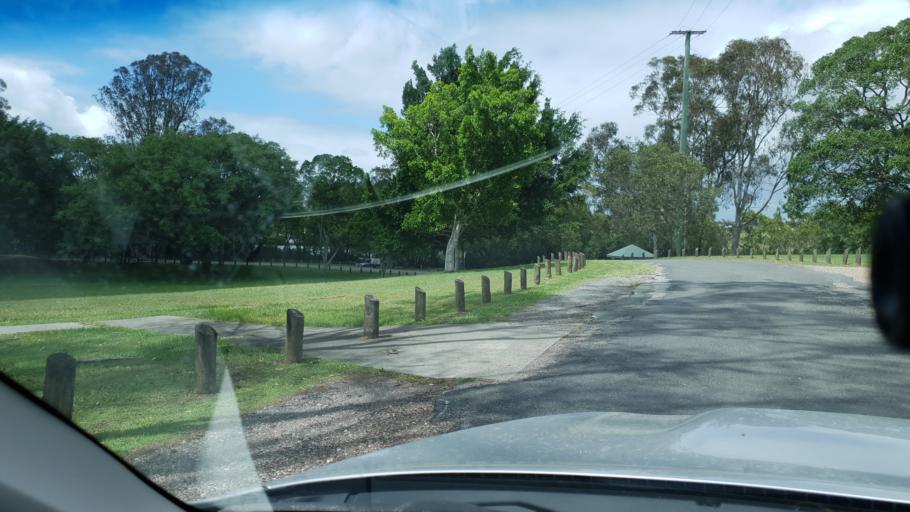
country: AU
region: Queensland
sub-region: Gold Coast
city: Yatala
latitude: -27.6794
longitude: 153.2263
